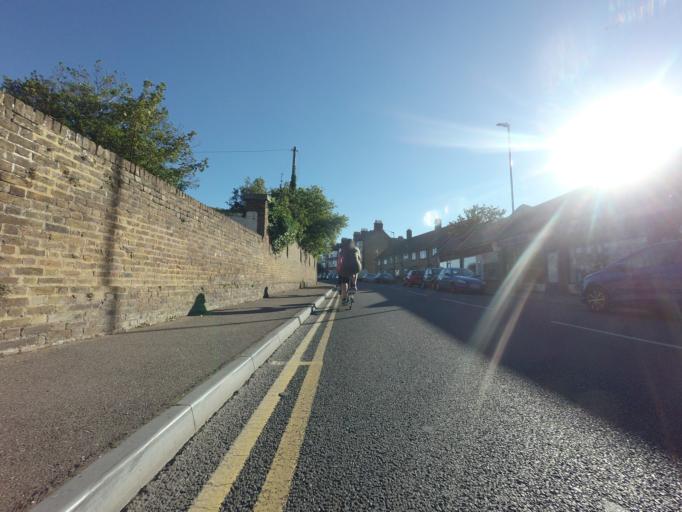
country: GB
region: England
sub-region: Kent
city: Herne Bay
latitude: 51.3707
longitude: 1.1151
